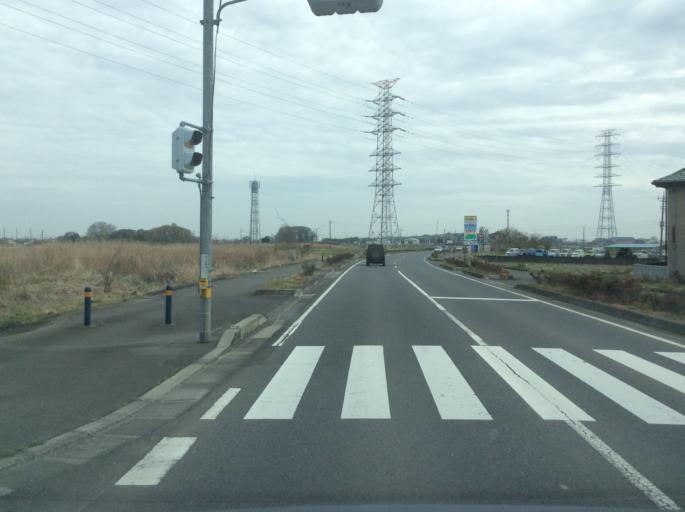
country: JP
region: Ibaraki
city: Ishige
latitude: 36.1743
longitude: 139.9545
